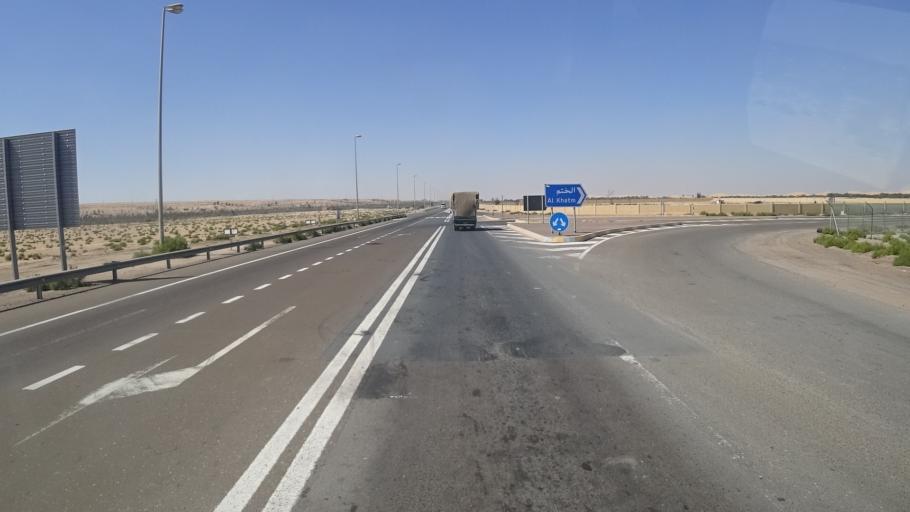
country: AE
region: Abu Dhabi
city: Al Ain
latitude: 24.1556
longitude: 55.0463
